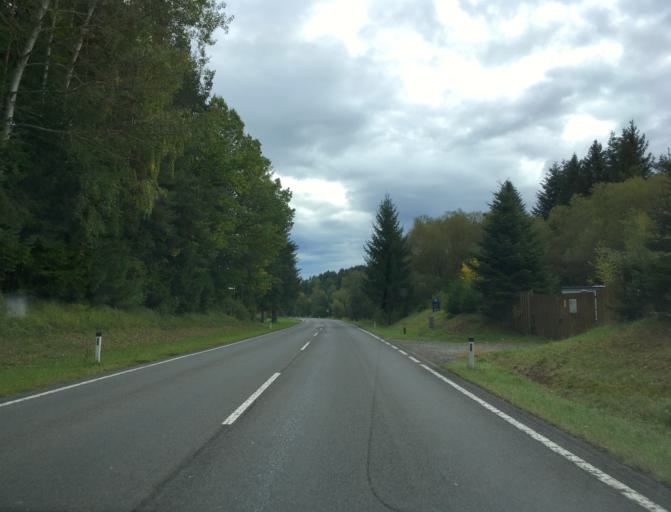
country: AT
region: Lower Austria
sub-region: Politischer Bezirk Neunkirchen
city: Thomasberg
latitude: 47.5346
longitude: 16.1711
